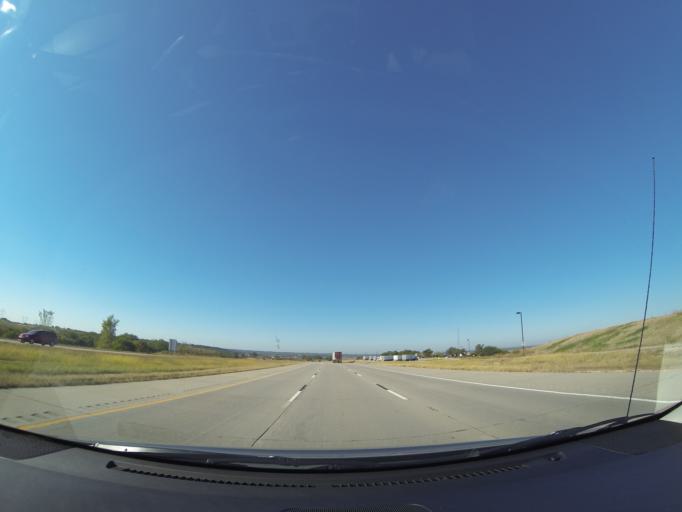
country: US
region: Nebraska
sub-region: Sarpy County
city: Gretna
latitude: 41.0854
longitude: -96.2720
